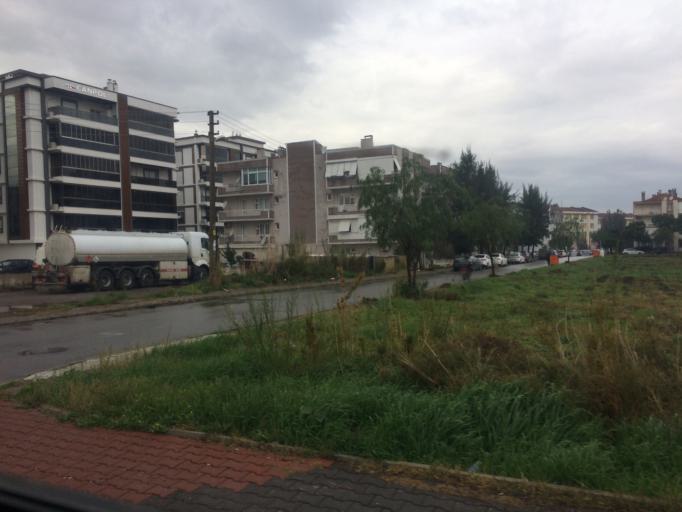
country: TR
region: Izmir
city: Karsiyaka
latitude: 38.4899
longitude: 27.0554
